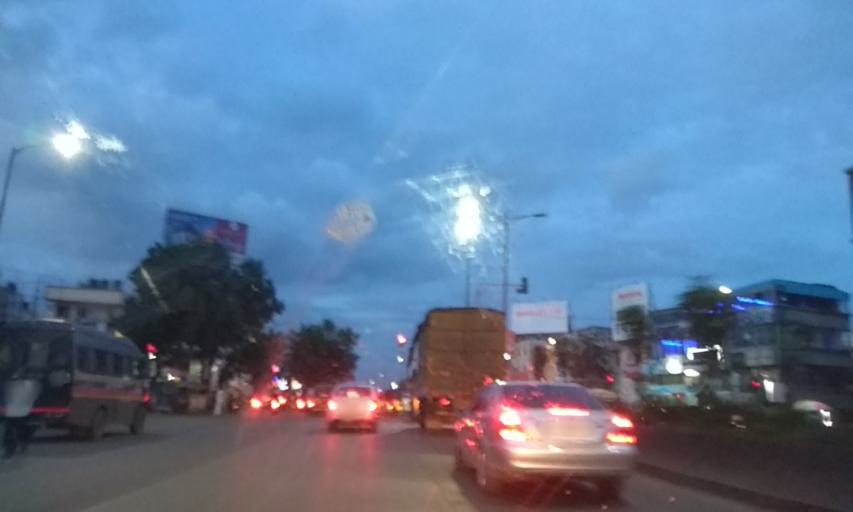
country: IN
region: Maharashtra
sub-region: Pune Division
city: Lohogaon
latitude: 18.5396
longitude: 73.9345
